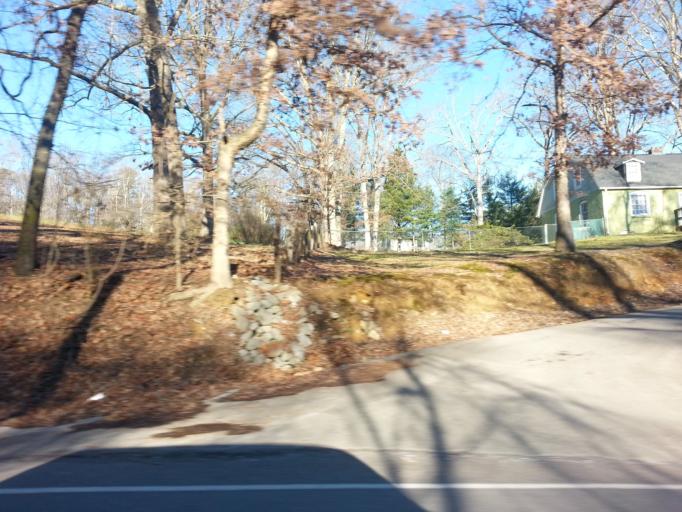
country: US
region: Tennessee
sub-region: Knox County
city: Farragut
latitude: 35.9508
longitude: -84.0620
